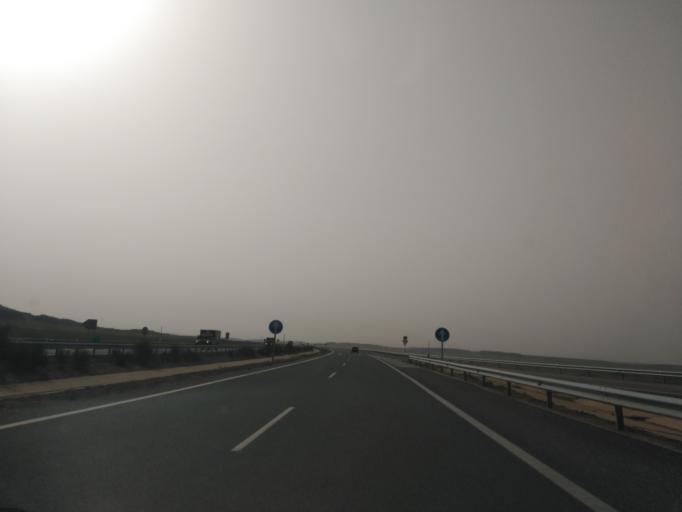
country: ES
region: Castille and Leon
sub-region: Provincia de Palencia
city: Pradanos de Ojeda
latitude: 42.6536
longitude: -4.3490
